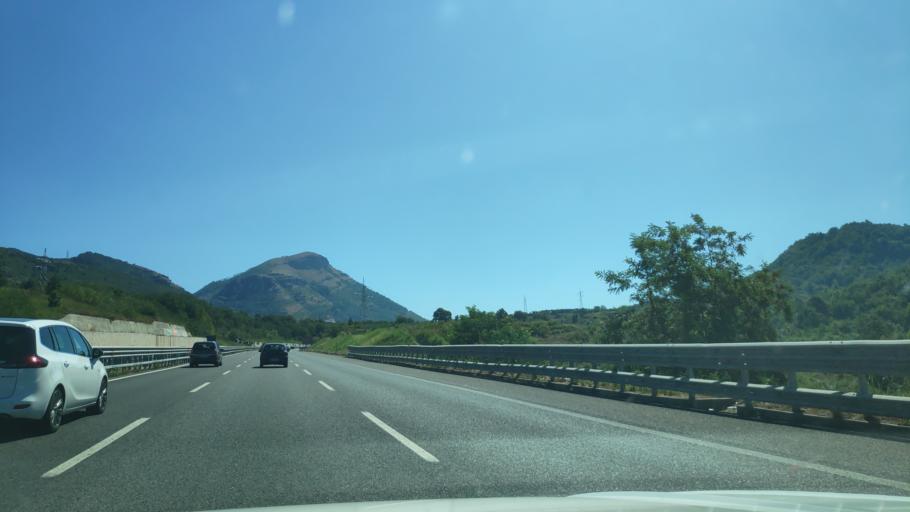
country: IT
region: Campania
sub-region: Provincia di Salerno
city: Piegolelle-San Bartolomeo
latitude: 40.6979
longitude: 14.8039
